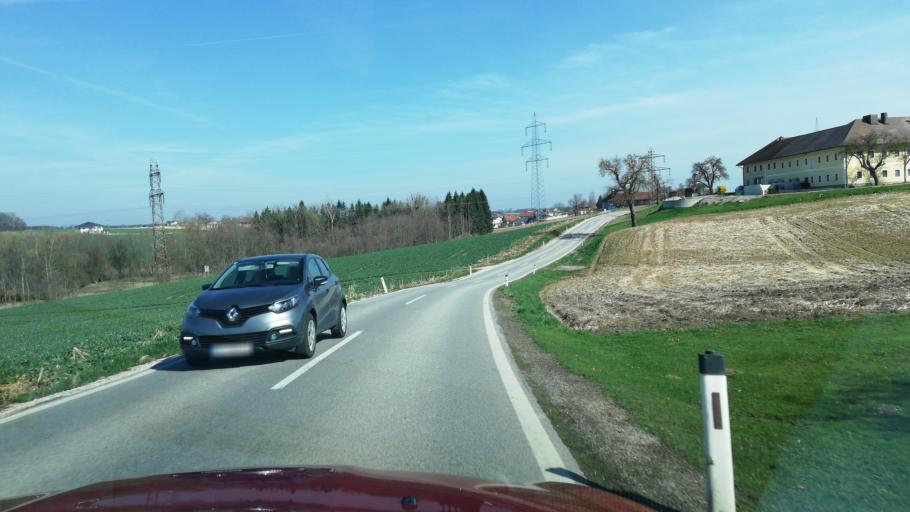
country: AT
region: Upper Austria
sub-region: Politischer Bezirk Kirchdorf an der Krems
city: Kremsmunster
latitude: 48.0889
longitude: 14.1093
